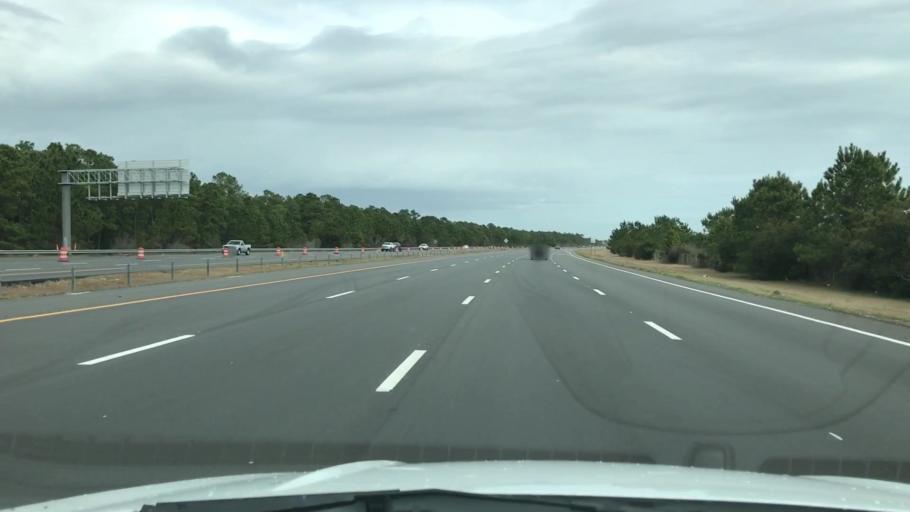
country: US
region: South Carolina
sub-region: Horry County
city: Socastee
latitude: 33.7094
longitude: -79.0087
